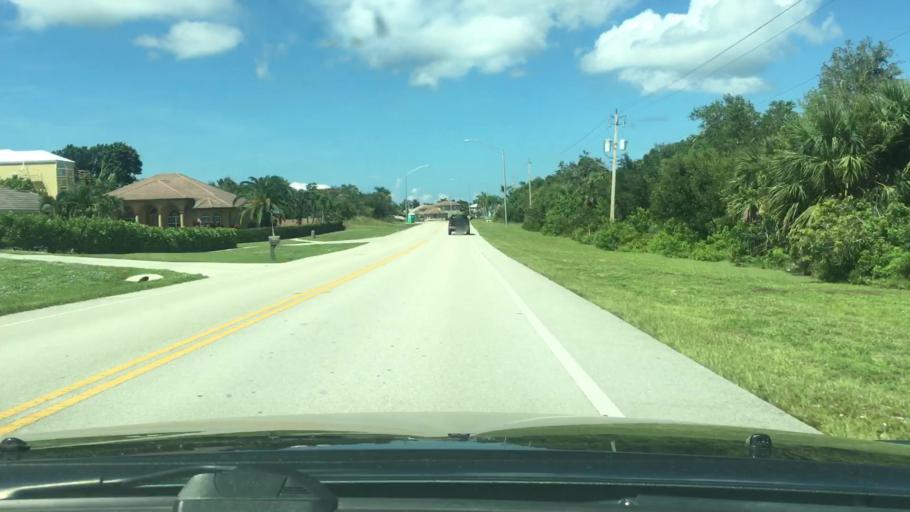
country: US
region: Florida
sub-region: Collier County
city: Marco
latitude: 25.9382
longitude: -81.6868
